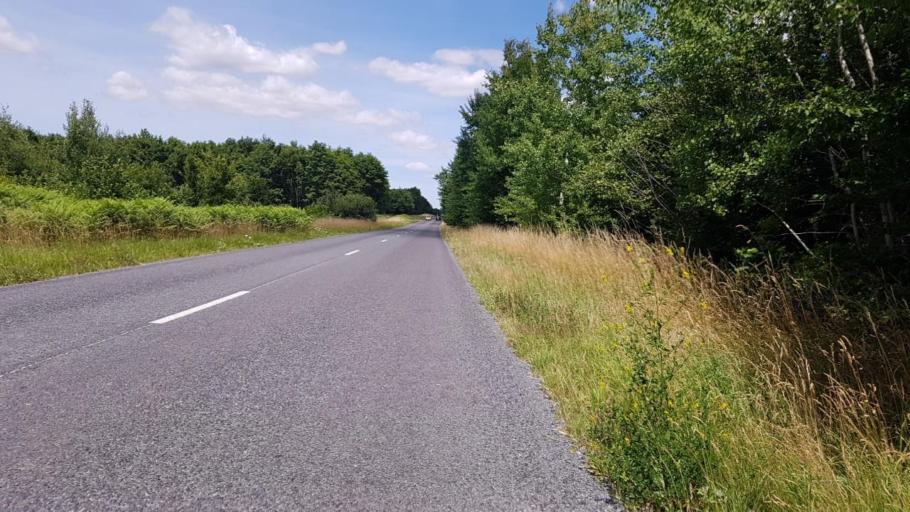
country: FR
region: Picardie
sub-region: Departement de l'Oise
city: Carlepont
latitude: 49.5245
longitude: 2.9837
